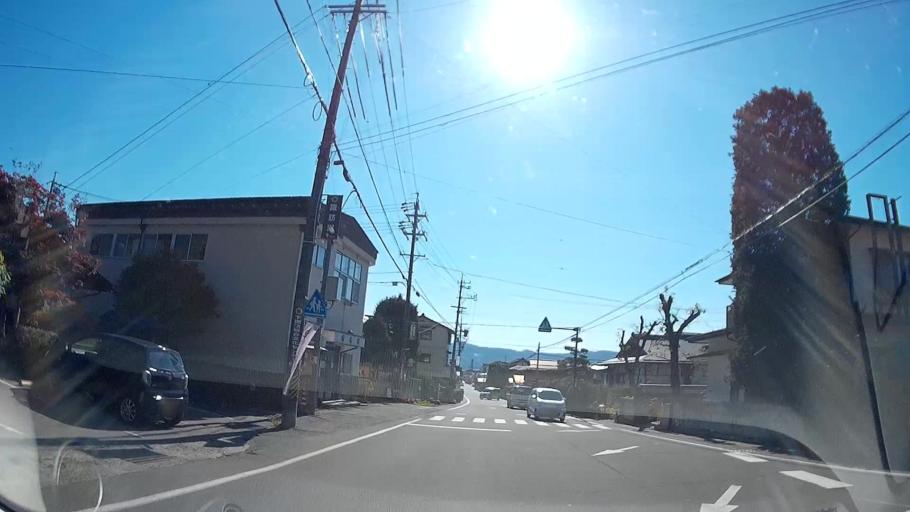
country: JP
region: Nagano
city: Okaya
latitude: 36.0800
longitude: 138.0819
